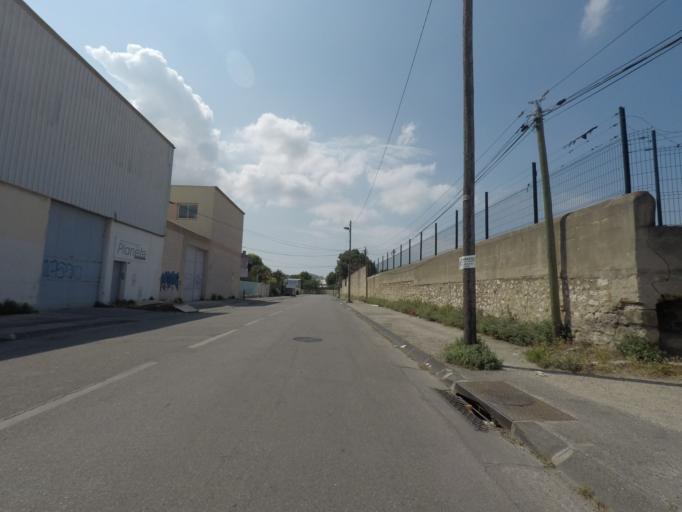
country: FR
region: Provence-Alpes-Cote d'Azur
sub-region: Departement des Bouches-du-Rhone
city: Marseille 10
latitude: 43.2759
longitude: 5.4048
